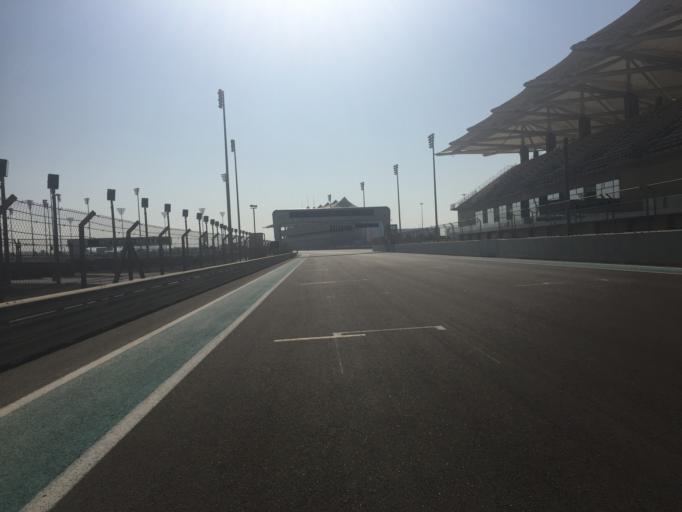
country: AE
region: Abu Dhabi
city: Abu Dhabi
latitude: 24.4655
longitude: 54.6045
